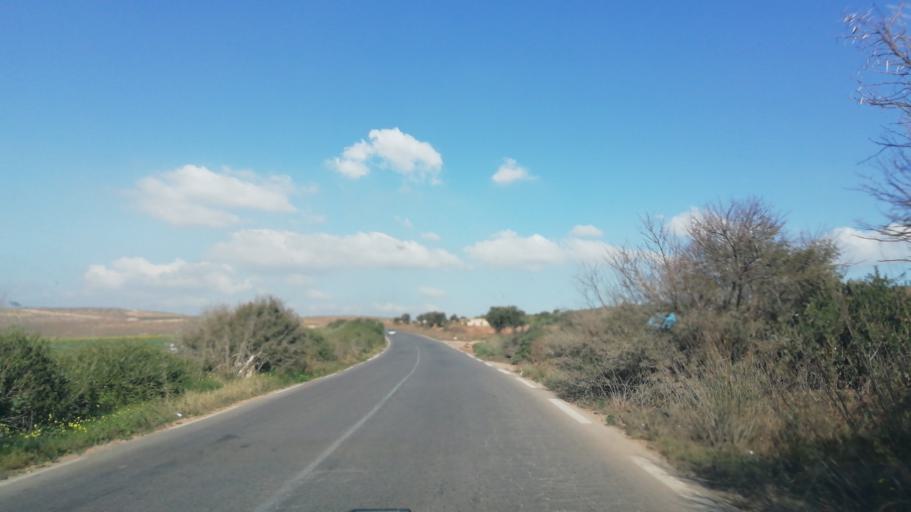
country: DZ
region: Oran
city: Ain el Bya
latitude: 35.7379
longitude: -0.2540
